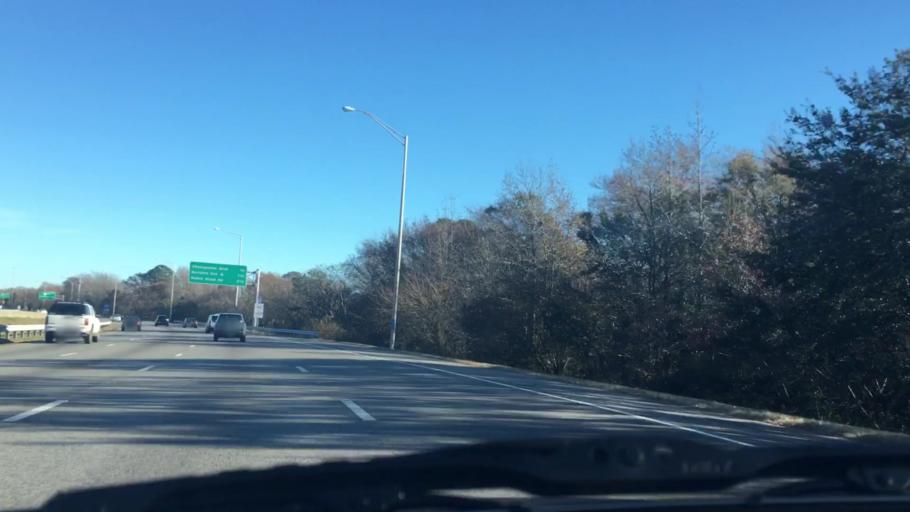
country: US
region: Virginia
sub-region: City of Norfolk
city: Norfolk
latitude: 36.9035
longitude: -76.2515
